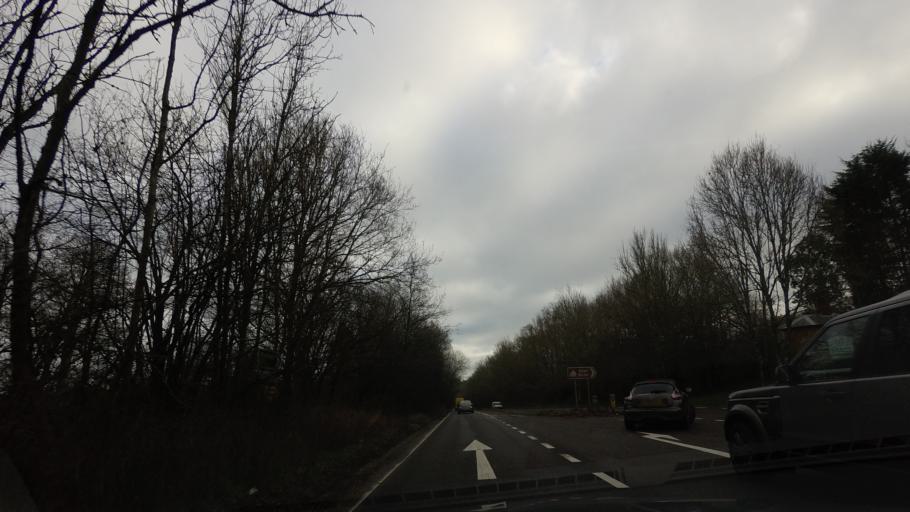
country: GB
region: England
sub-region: East Sussex
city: Wadhurst
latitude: 51.0879
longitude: 0.4012
